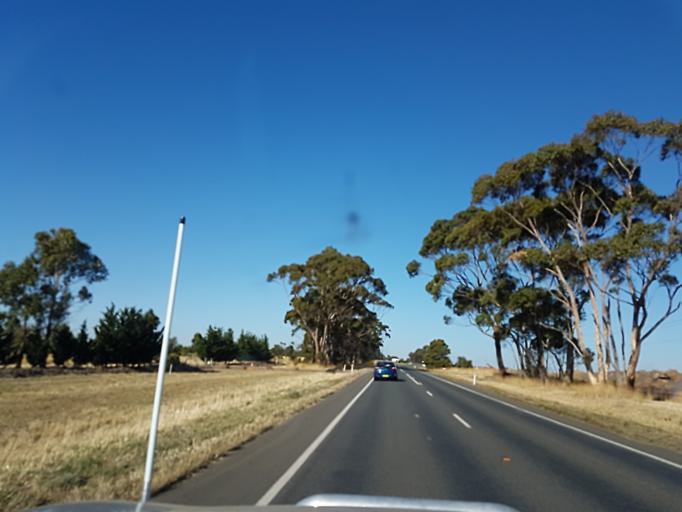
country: AU
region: Victoria
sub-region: Surf Coast
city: Anglesea
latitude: -38.2540
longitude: 143.9542
